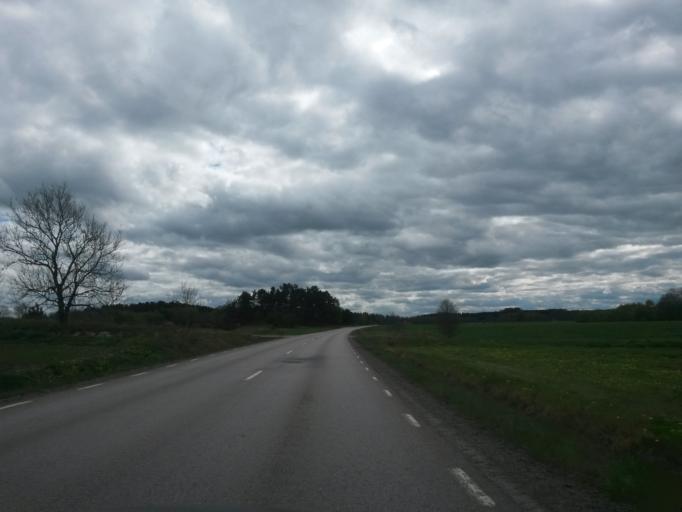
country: SE
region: Vaestra Goetaland
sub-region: Essunga Kommun
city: Nossebro
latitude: 58.2124
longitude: 12.7175
